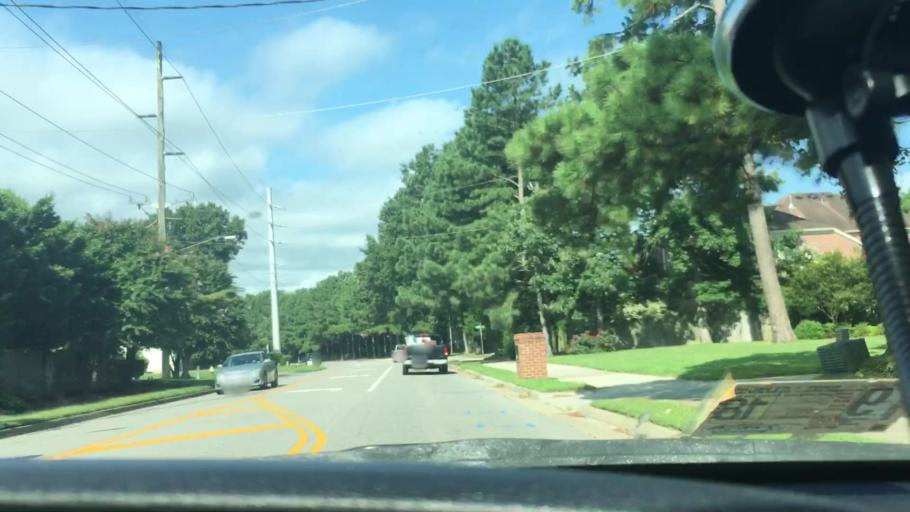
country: US
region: Virginia
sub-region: City of Virginia Beach
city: Virginia Beach
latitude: 36.8797
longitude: -76.0381
